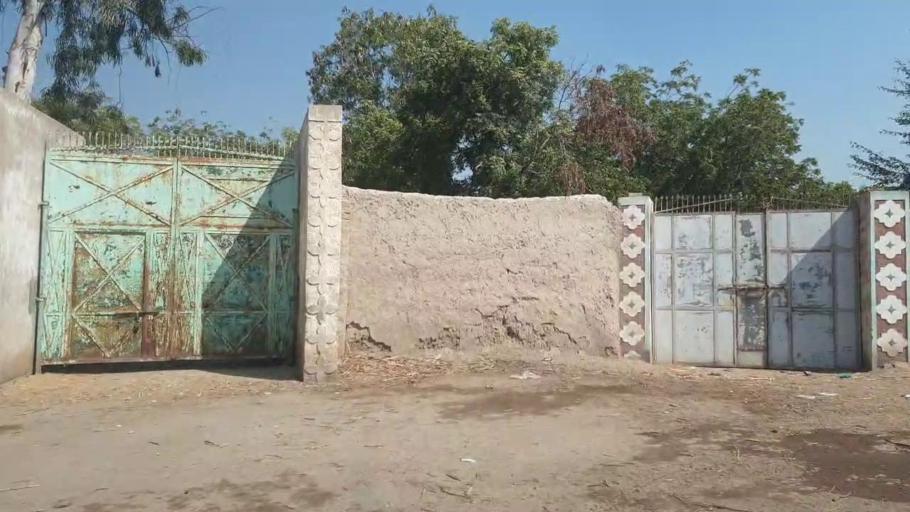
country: PK
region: Sindh
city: Tando Jam
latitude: 25.3247
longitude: 68.6333
